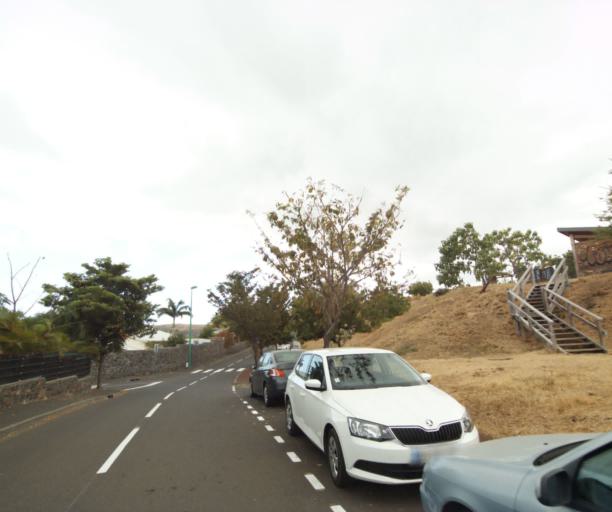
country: RE
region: Reunion
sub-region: Reunion
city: Saint-Paul
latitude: -21.0612
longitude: 55.2258
